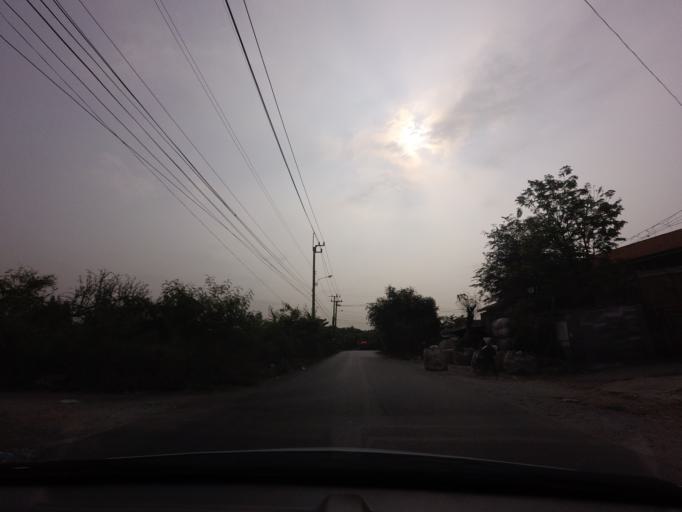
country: TH
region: Bangkok
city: Nong Khaem
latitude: 13.7360
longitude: 100.3545
